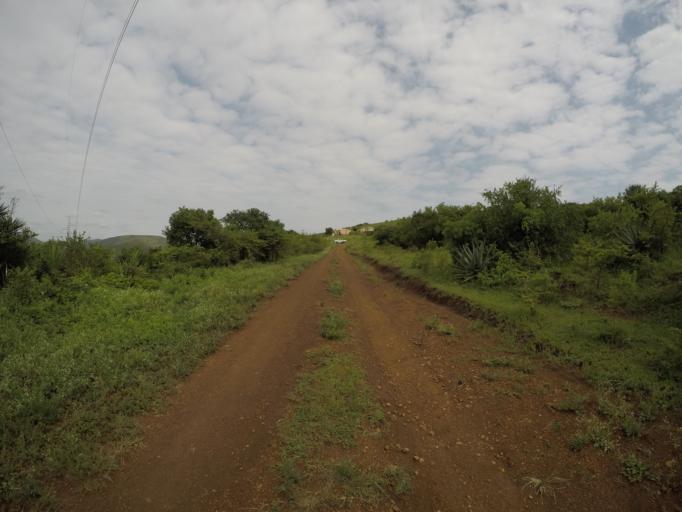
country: ZA
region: KwaZulu-Natal
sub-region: uThungulu District Municipality
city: Empangeni
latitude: -28.6279
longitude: 31.9044
